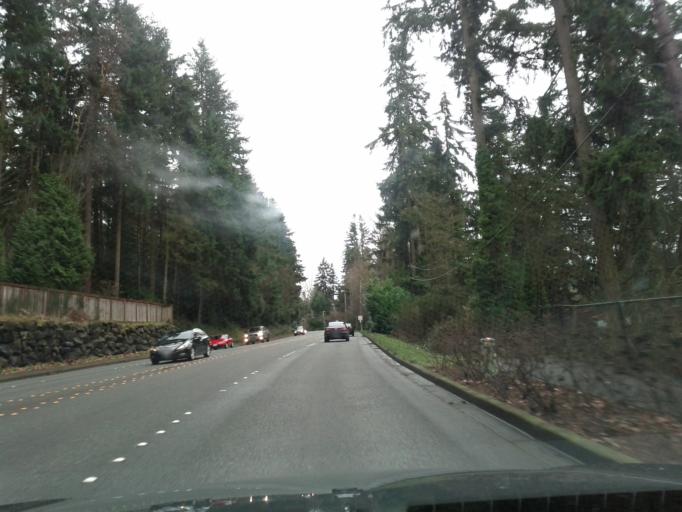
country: US
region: Washington
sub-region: King County
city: Eastgate
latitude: 47.5748
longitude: -122.1404
